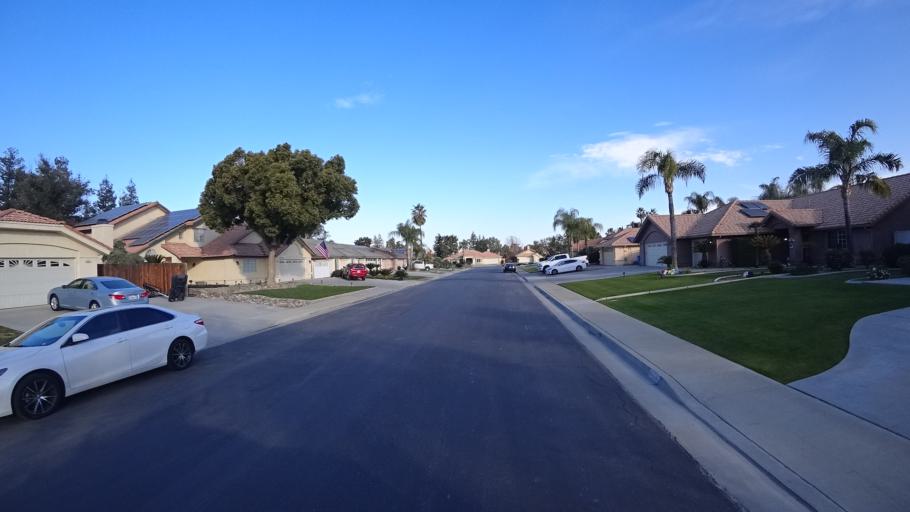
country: US
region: California
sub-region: Kern County
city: Rosedale
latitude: 35.3478
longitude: -119.1583
